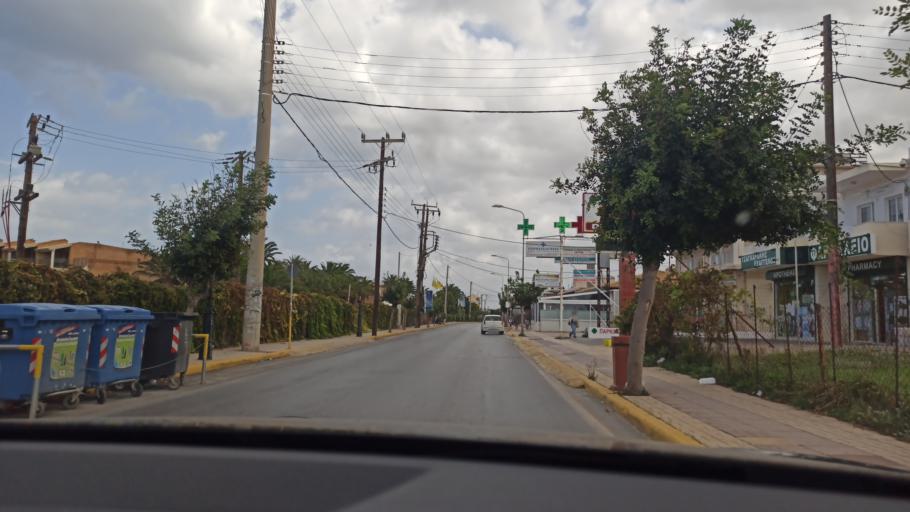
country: GR
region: Crete
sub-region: Nomos Irakleiou
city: Gazi
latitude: 35.3356
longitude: 25.0830
